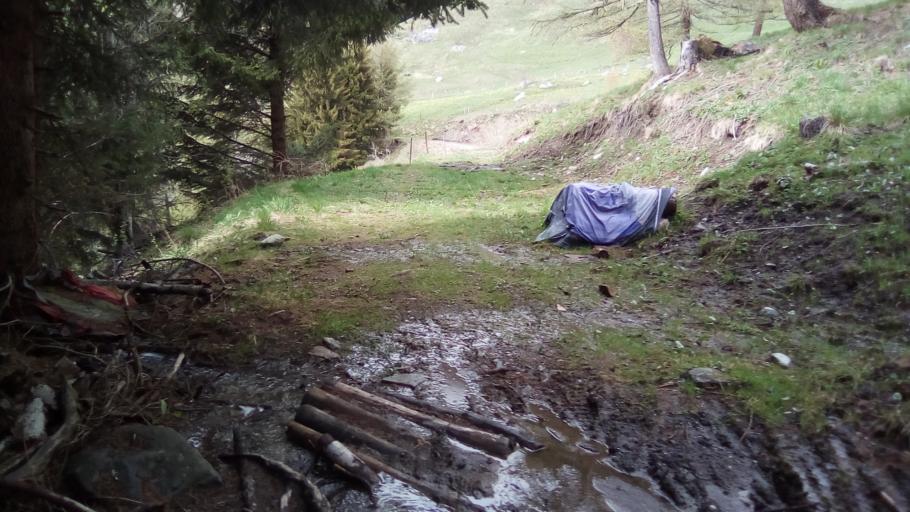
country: CH
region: Valais
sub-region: Entremont District
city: Orsieres
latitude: 46.0232
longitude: 7.1787
